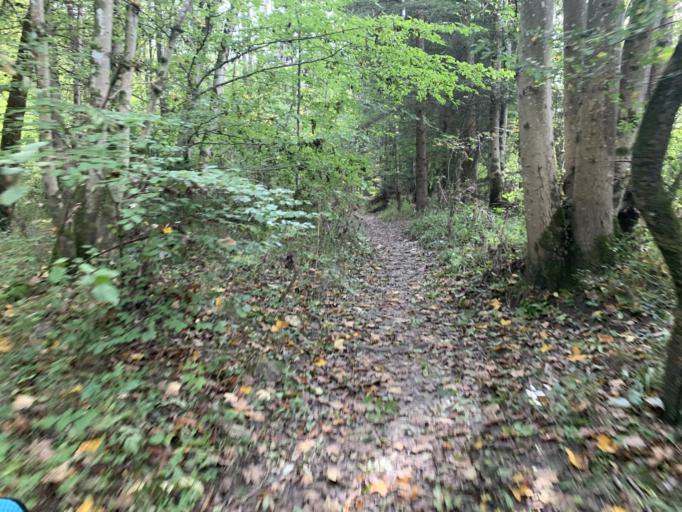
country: DE
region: Bavaria
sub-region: Upper Bavaria
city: Grunwald
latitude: 48.0284
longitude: 11.5082
